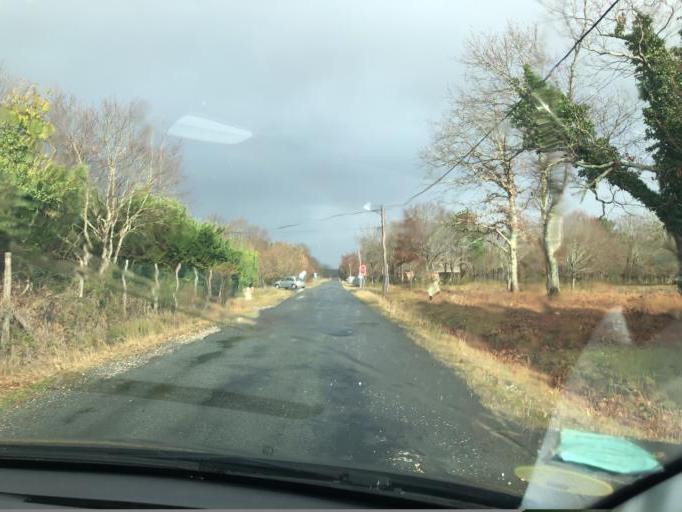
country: FR
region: Aquitaine
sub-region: Departement de la Gironde
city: Hourtin
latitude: 45.1767
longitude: -1.0511
